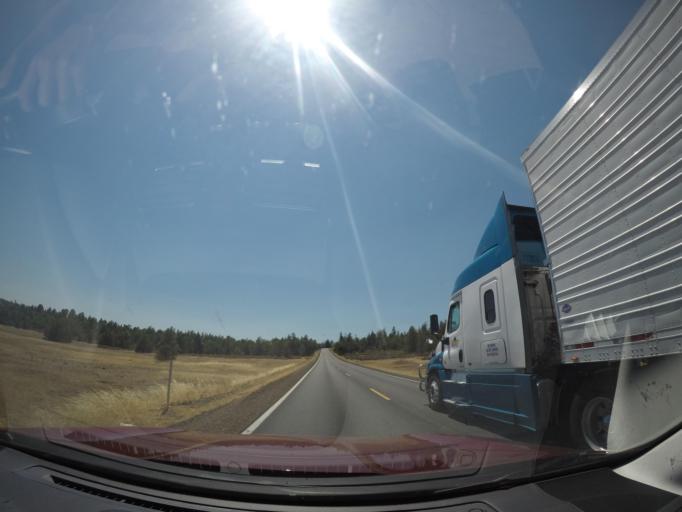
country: US
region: California
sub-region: Shasta County
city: Burney
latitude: 40.9942
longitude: -121.4663
